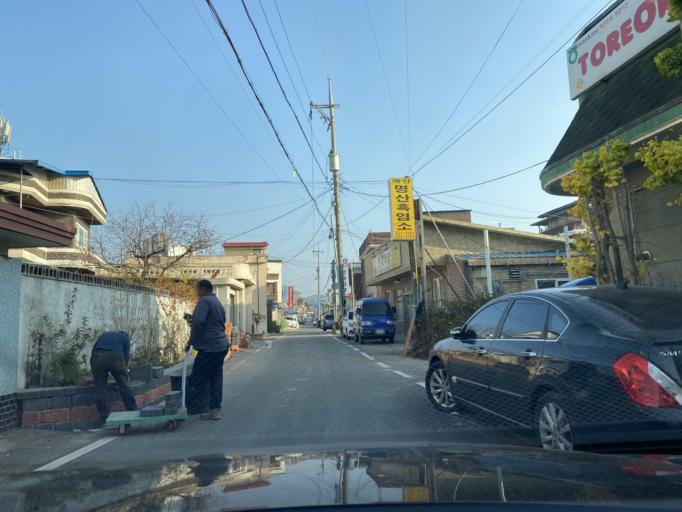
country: KR
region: Chungcheongnam-do
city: Yesan
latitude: 36.6831
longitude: 126.8296
